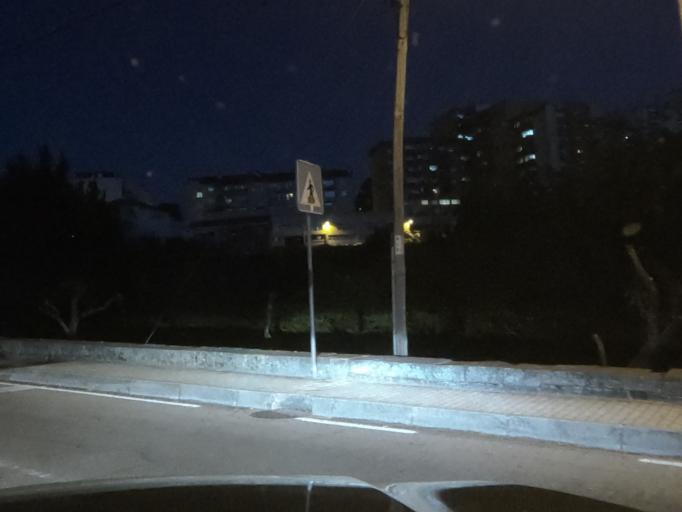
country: PT
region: Vila Real
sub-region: Vila Real
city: Vila Real
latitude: 41.2963
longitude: -7.7507
